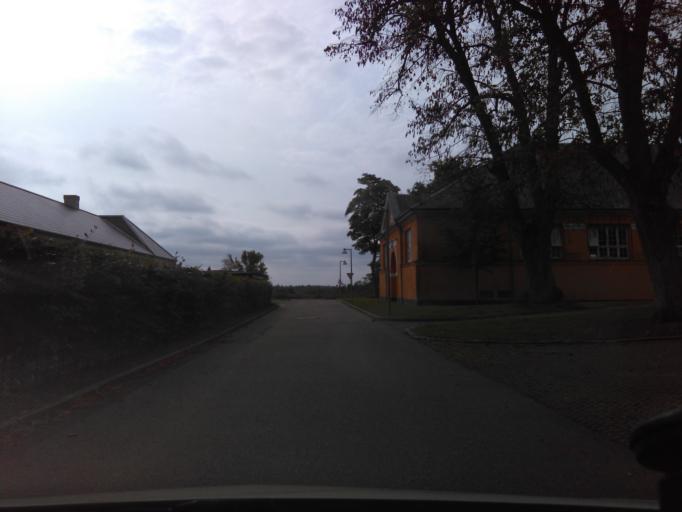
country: DK
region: Capital Region
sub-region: Ballerup Kommune
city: Malov
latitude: 55.7754
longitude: 12.3229
